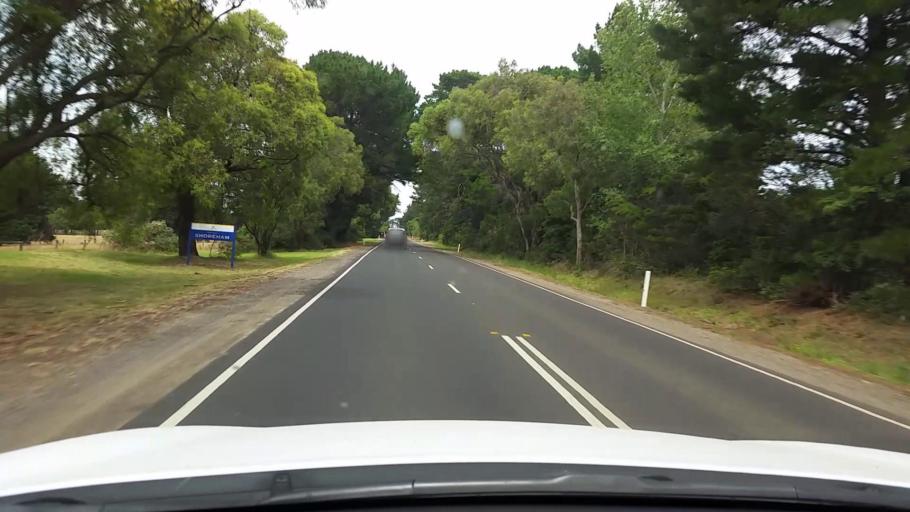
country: AU
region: Victoria
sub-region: Mornington Peninsula
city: Merricks
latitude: -38.4093
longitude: 145.0616
